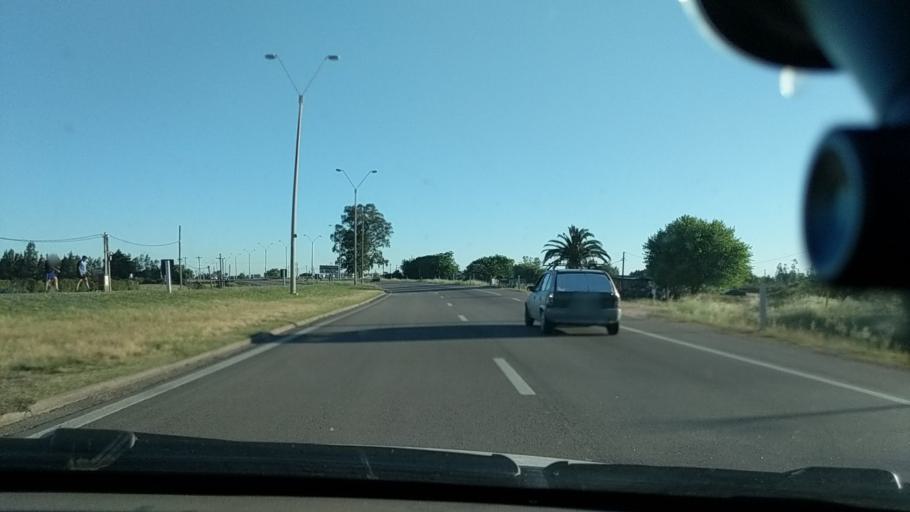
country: UY
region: Canelones
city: Joanico
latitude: -34.6114
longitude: -56.2605
